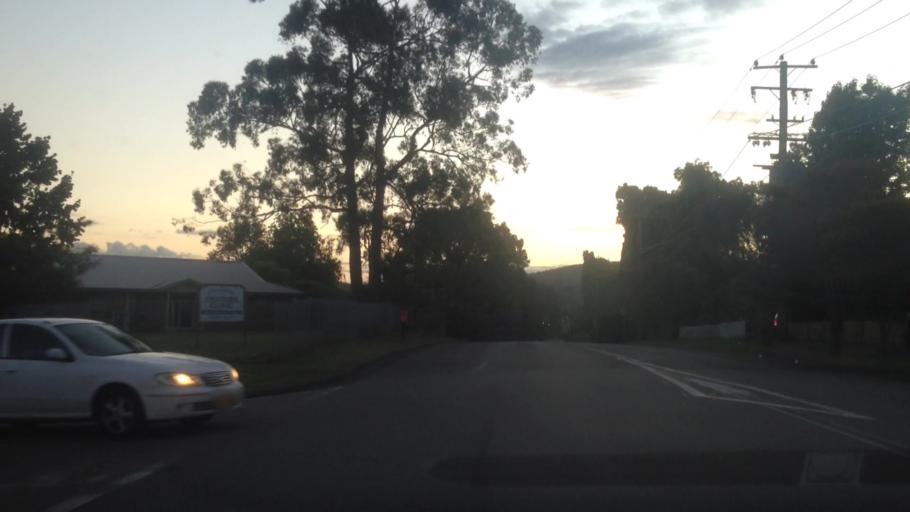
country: AU
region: New South Wales
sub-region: Lake Macquarie Shire
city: Cooranbong
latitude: -33.0703
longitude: 151.4632
